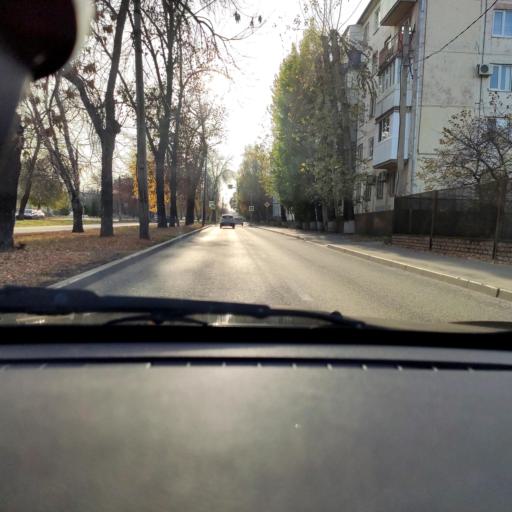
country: RU
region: Samara
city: Tol'yatti
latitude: 53.5219
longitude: 49.3995
